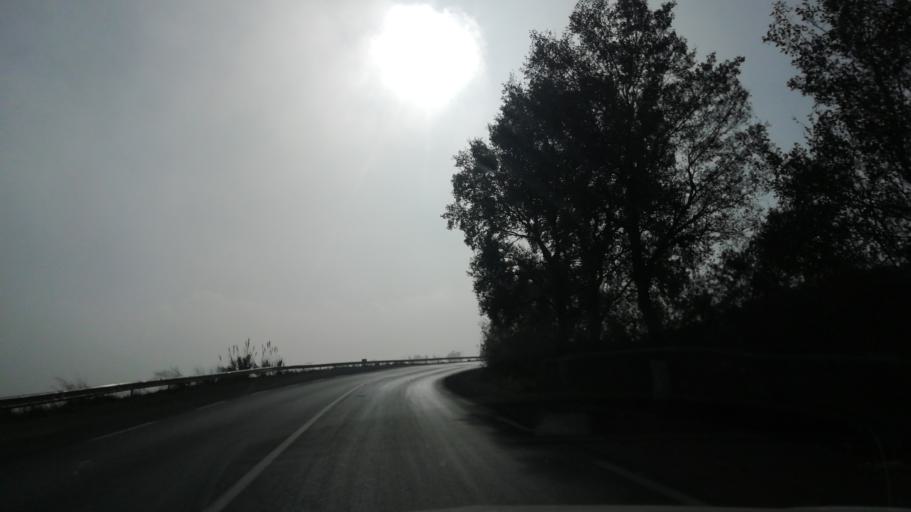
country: DZ
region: Mascara
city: Mascara
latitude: 35.5316
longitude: 0.3541
